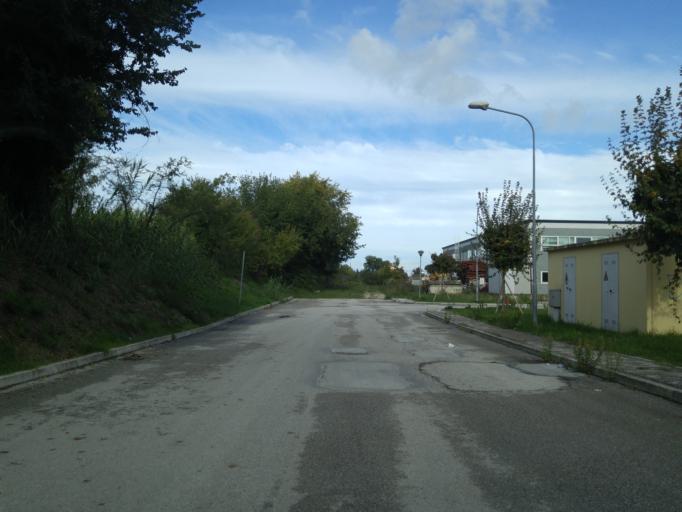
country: IT
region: The Marches
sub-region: Provincia di Pesaro e Urbino
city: Calcinelli
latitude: 43.7557
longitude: 12.9239
